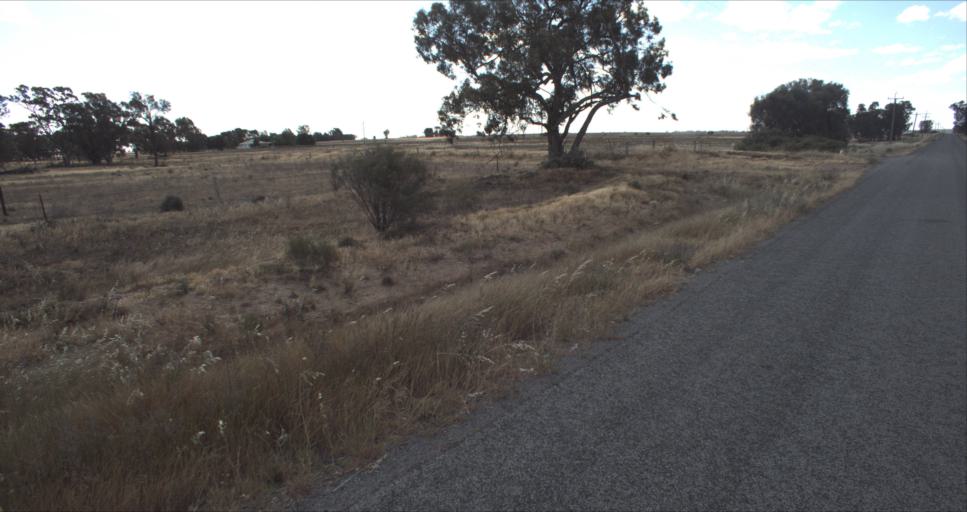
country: AU
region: New South Wales
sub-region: Leeton
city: Leeton
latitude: -34.4884
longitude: 146.2477
